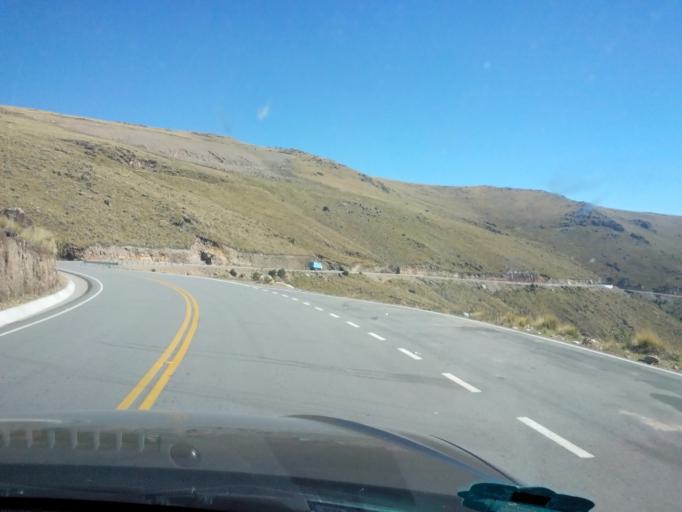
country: PE
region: Ayacucho
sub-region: Provincia de Huamanga
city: Ocros
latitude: -13.3896
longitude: -73.9530
